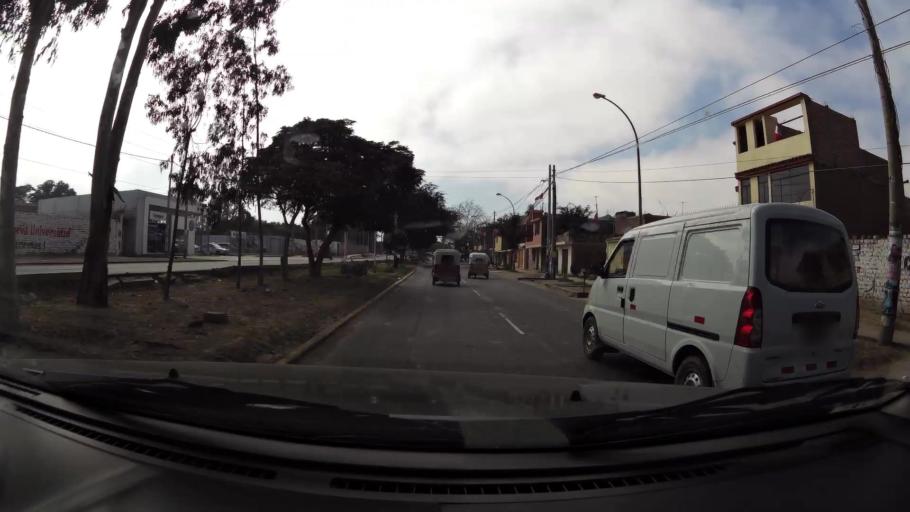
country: PE
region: Ica
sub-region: Provincia de Ica
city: Ica
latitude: -14.0766
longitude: -75.7371
